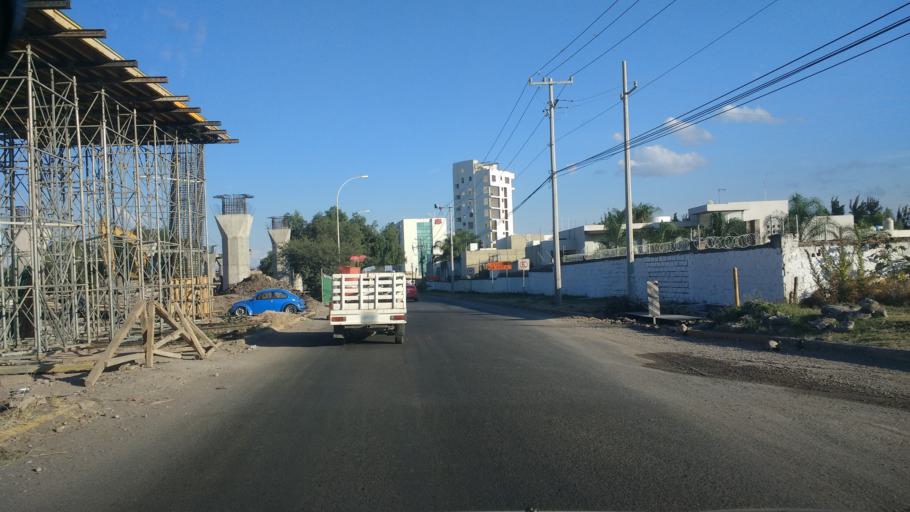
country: MX
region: Guanajuato
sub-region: Leon
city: La Ermita
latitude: 21.1689
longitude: -101.6962
